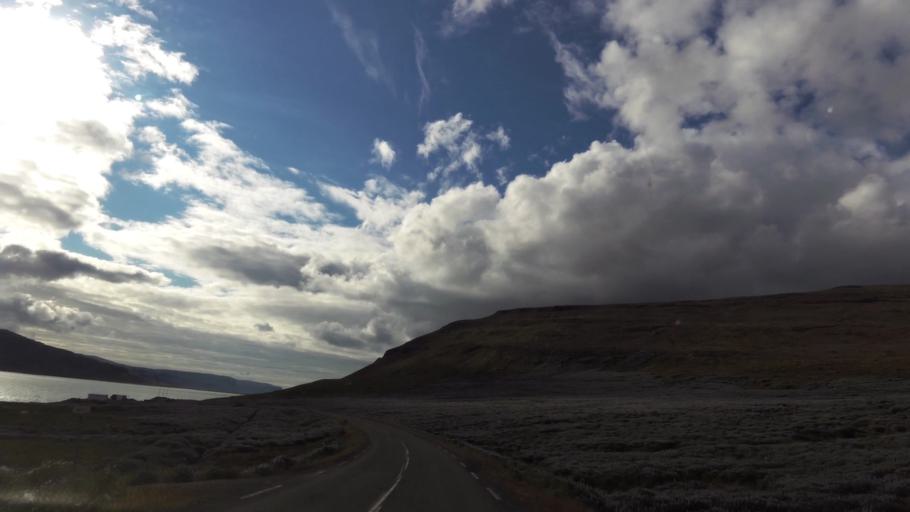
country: IS
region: West
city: Olafsvik
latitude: 65.5423
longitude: -23.8722
